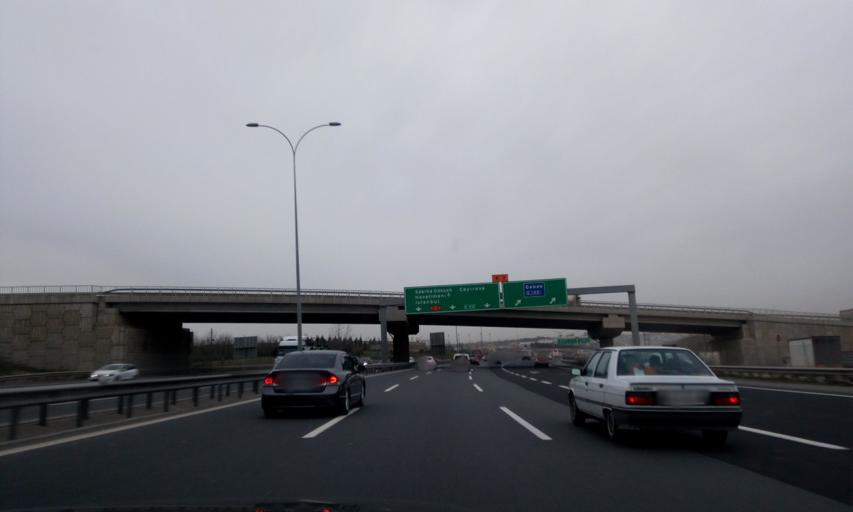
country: TR
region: Kocaeli
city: Tavsanli
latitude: 40.8052
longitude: 29.4845
